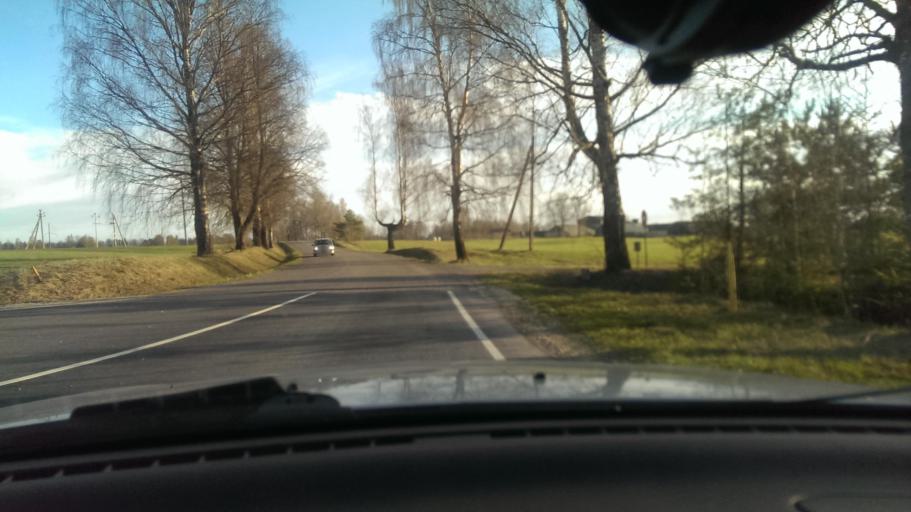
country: EE
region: Vorumaa
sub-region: Antsla vald
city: Vana-Antsla
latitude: 57.9969
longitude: 26.7632
